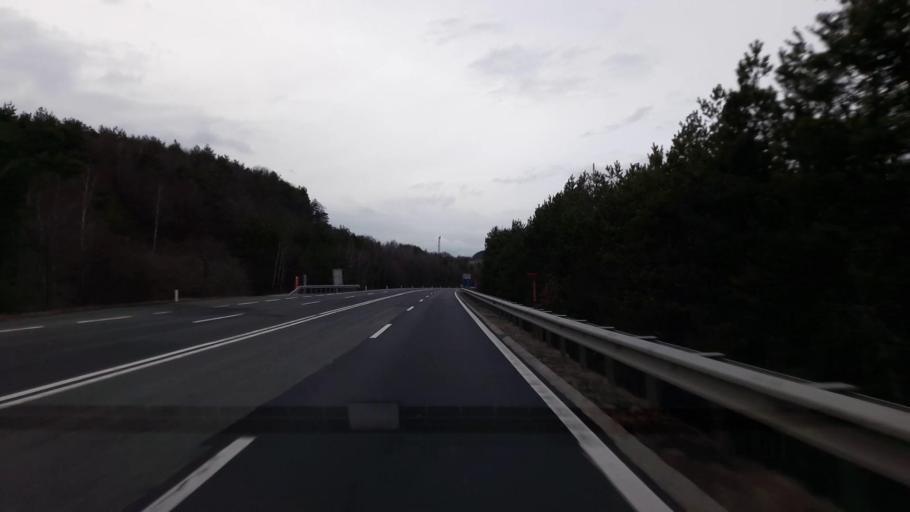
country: AT
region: Burgenland
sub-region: Politischer Bezirk Mattersburg
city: Sieggraben
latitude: 47.6425
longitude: 16.3758
